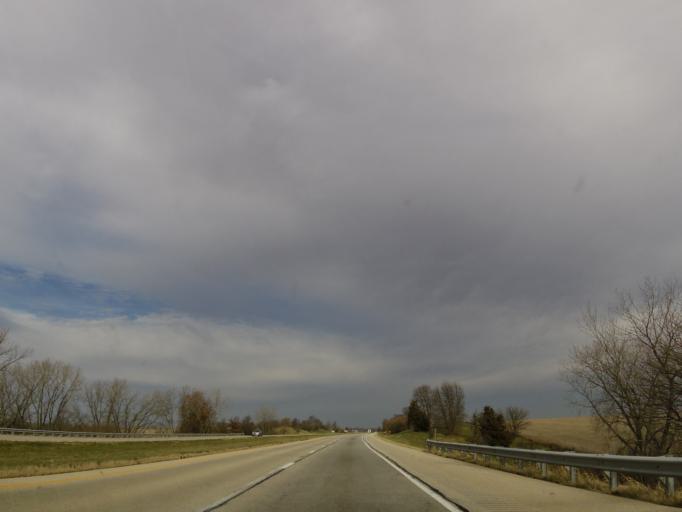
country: US
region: Illinois
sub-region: Henry County
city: Orion
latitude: 41.2378
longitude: -90.3316
